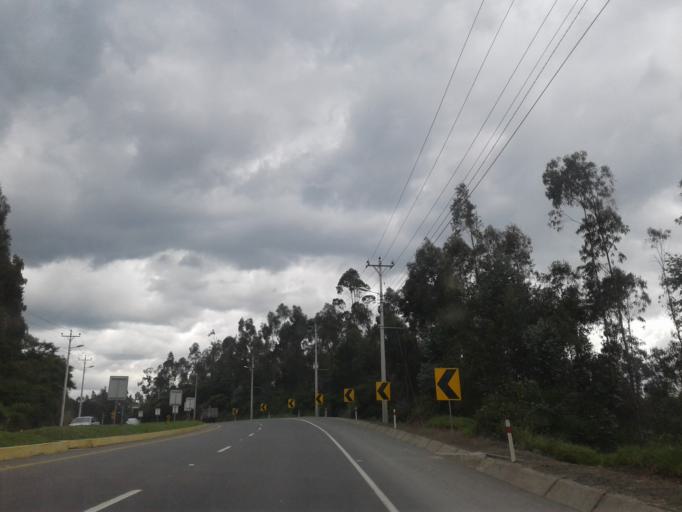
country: EC
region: Pichincha
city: Sangolqui
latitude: -0.3186
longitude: -78.3697
